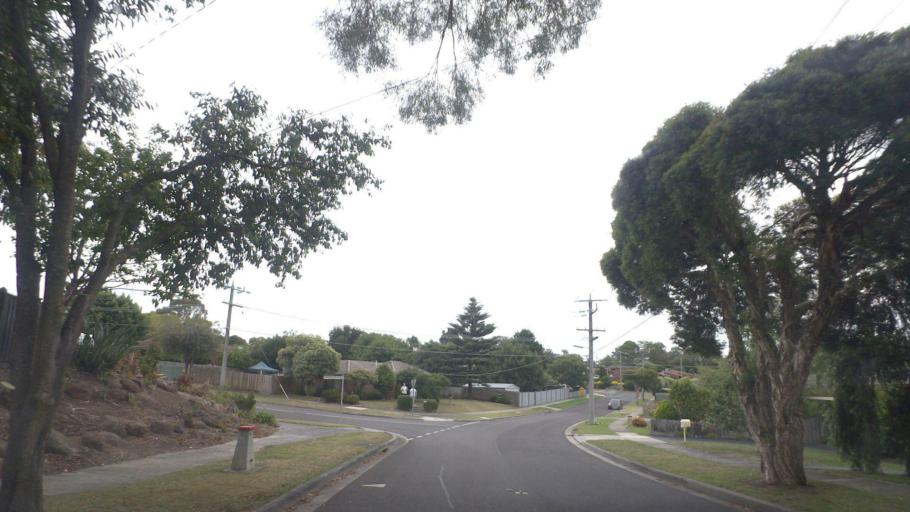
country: AU
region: Victoria
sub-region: Yarra Ranges
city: Kilsyth
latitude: -37.7973
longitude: 145.3299
